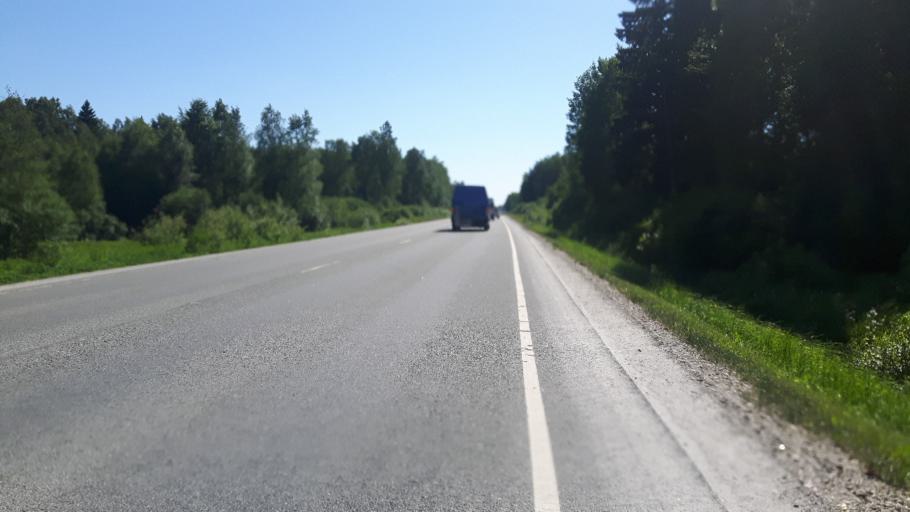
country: EE
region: Raplamaa
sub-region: Rapla vald
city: Rapla
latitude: 59.0238
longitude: 24.8123
